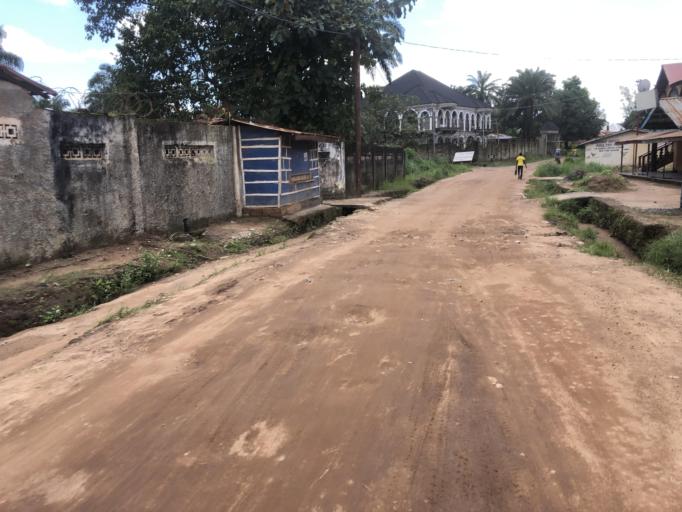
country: SL
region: Northern Province
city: Makeni
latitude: 8.8615
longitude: -12.0495
